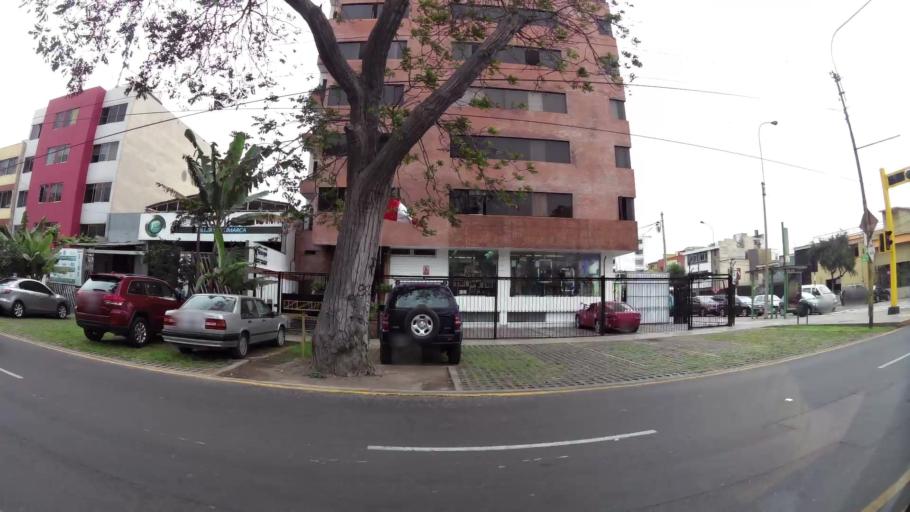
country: PE
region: Lima
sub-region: Lima
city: Surco
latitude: -12.1306
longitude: -77.0180
